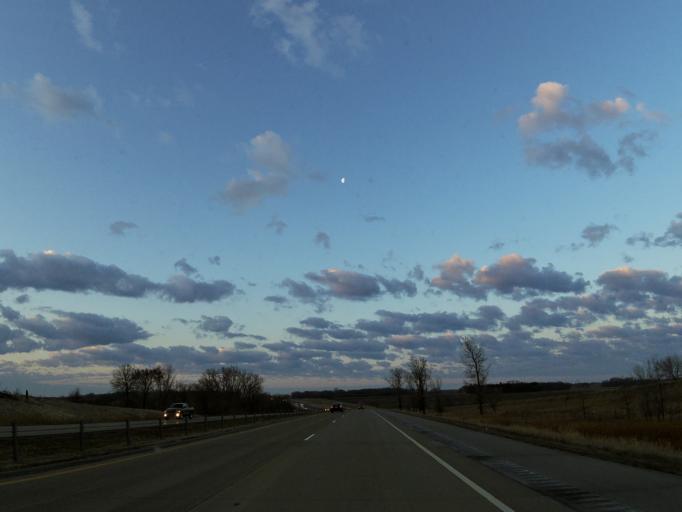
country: US
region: Minnesota
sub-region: Scott County
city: Elko New Market
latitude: 44.5040
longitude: -93.2901
